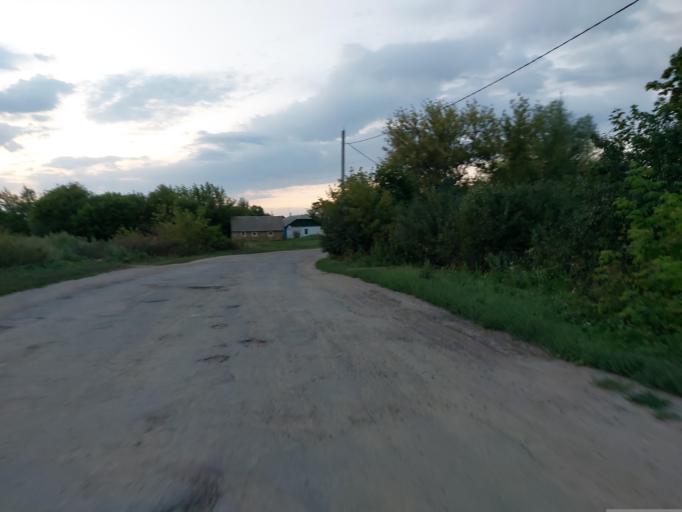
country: RU
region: Lipetsk
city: Dolgorukovo
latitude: 52.3756
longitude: 38.0516
